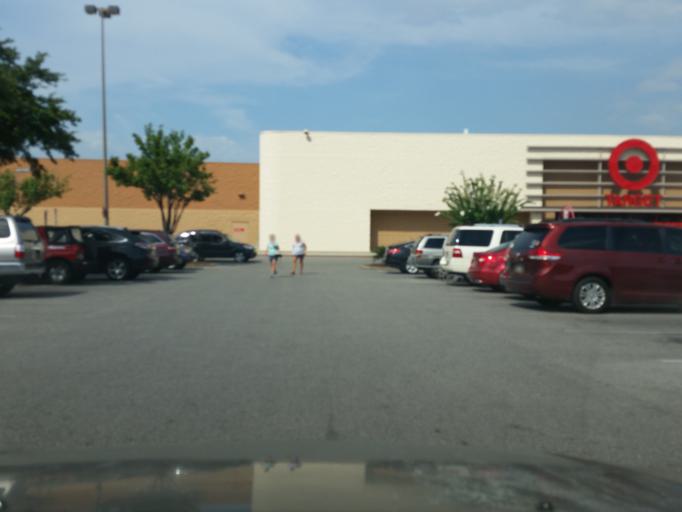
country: US
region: Florida
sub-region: Escambia County
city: Brent
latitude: 30.4691
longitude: -87.2081
